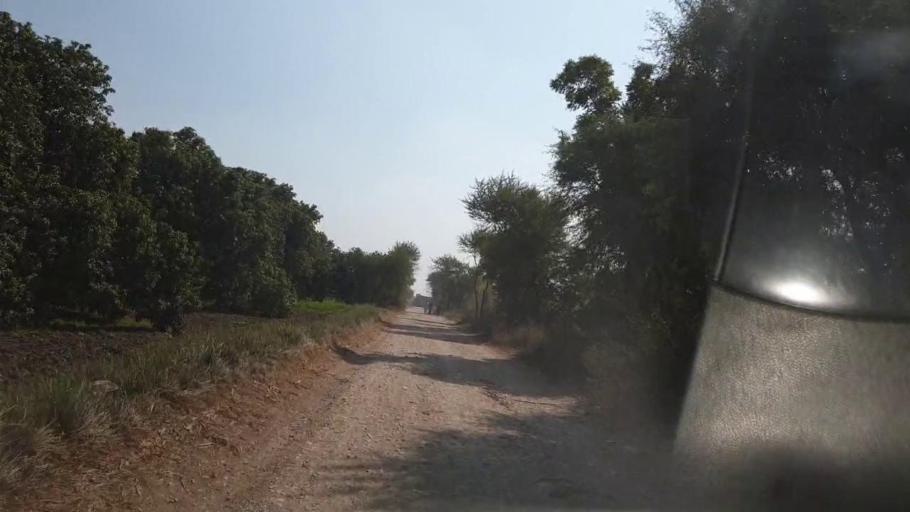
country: PK
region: Sindh
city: Matiari
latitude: 25.5058
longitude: 68.4657
